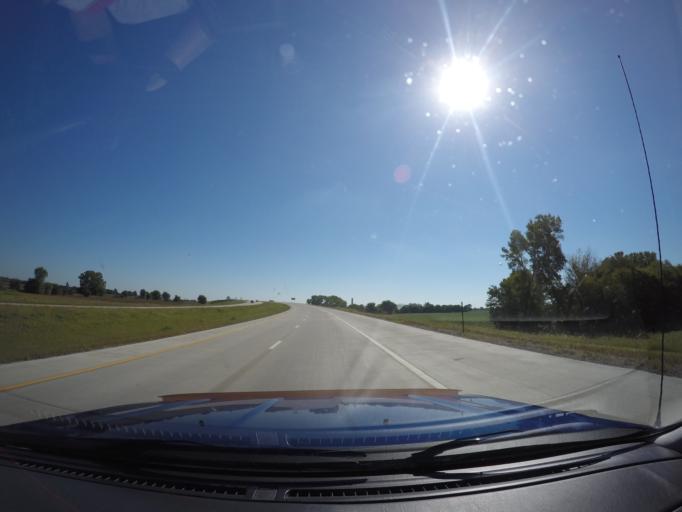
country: US
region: Kansas
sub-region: Shawnee County
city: Topeka
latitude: 39.0905
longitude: -95.7625
